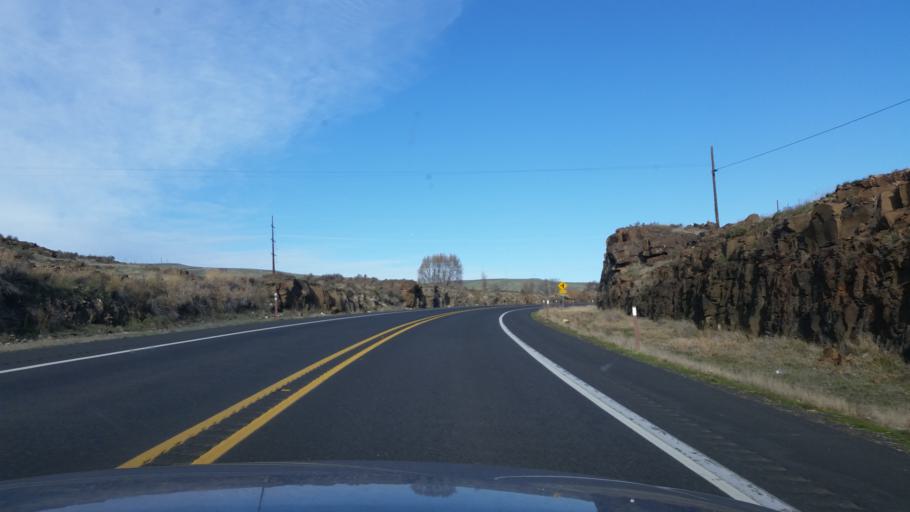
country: US
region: Washington
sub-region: Grant County
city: Ephrata
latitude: 47.2790
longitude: -119.5806
